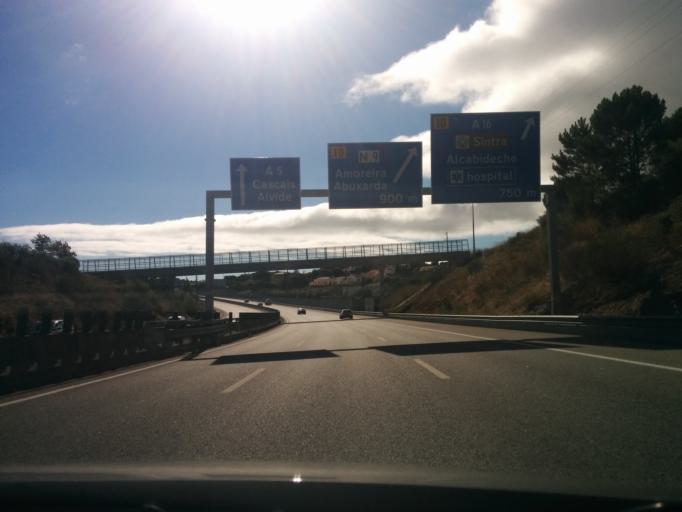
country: PT
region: Lisbon
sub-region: Cascais
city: Alcabideche
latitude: 38.7270
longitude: -9.4055
